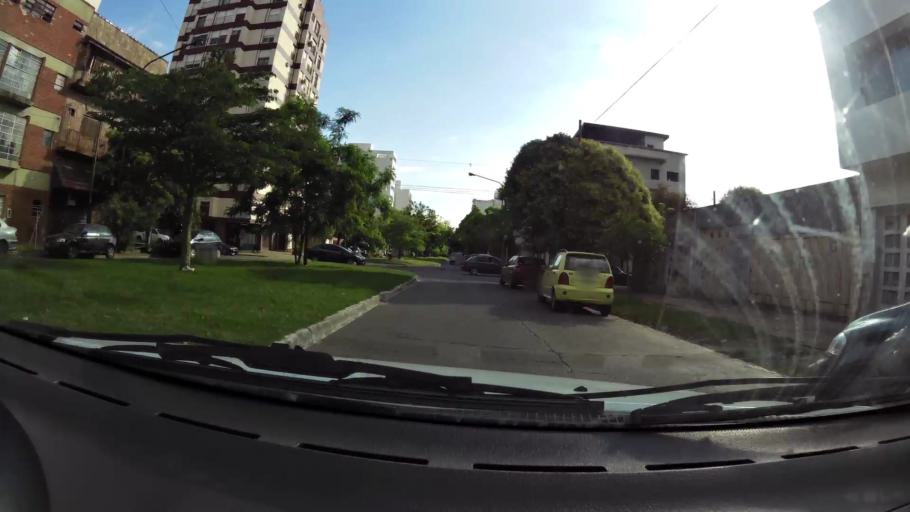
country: AR
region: Buenos Aires
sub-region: Partido de La Plata
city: La Plata
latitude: -34.9027
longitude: -57.9589
